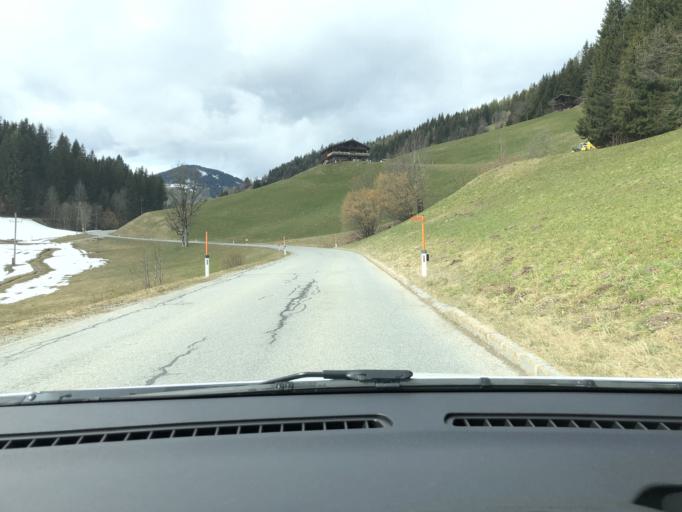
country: AT
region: Tyrol
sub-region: Politischer Bezirk Kitzbuhel
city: Itter
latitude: 47.4491
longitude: 12.1205
